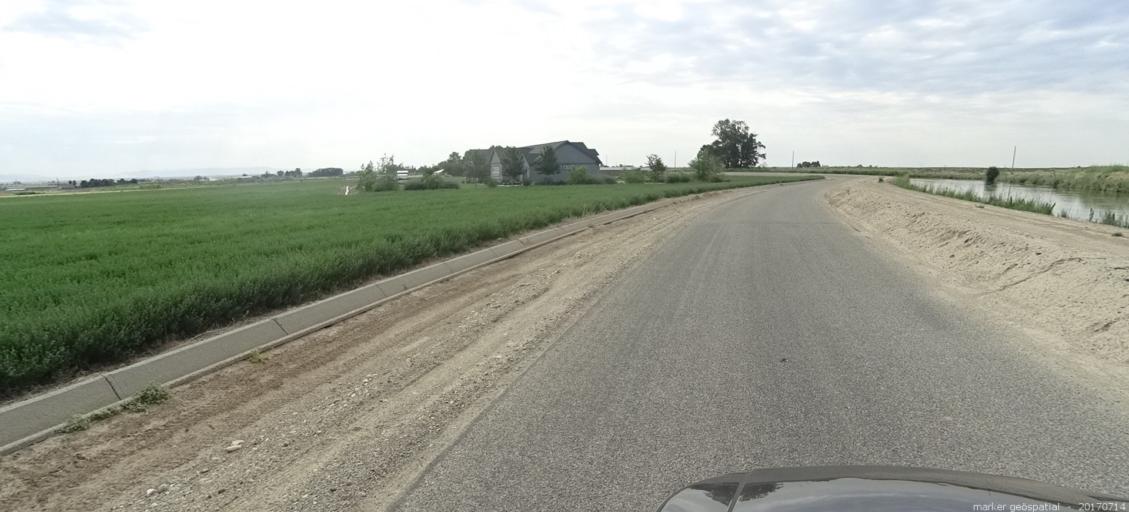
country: US
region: Idaho
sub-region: Ada County
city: Kuna
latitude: 43.4615
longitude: -116.3693
